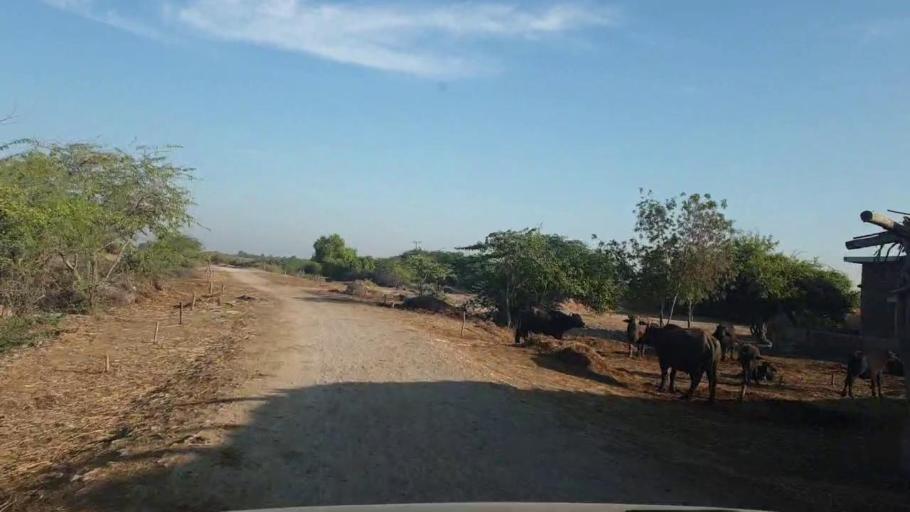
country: PK
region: Sindh
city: Talhar
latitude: 24.8164
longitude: 68.8400
